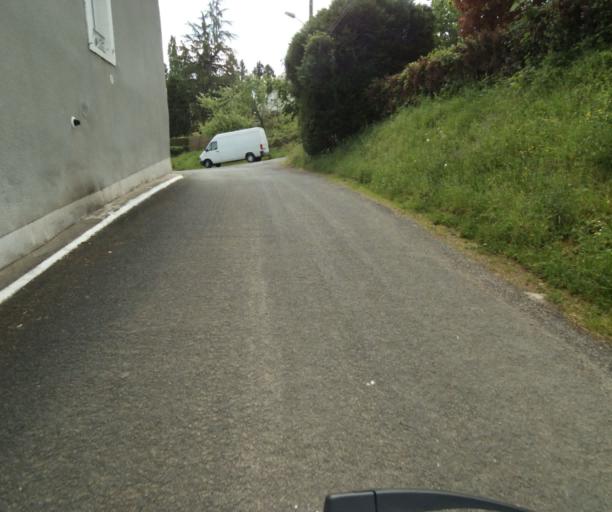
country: FR
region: Limousin
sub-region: Departement de la Correze
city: Tulle
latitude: 45.2727
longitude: 1.7606
